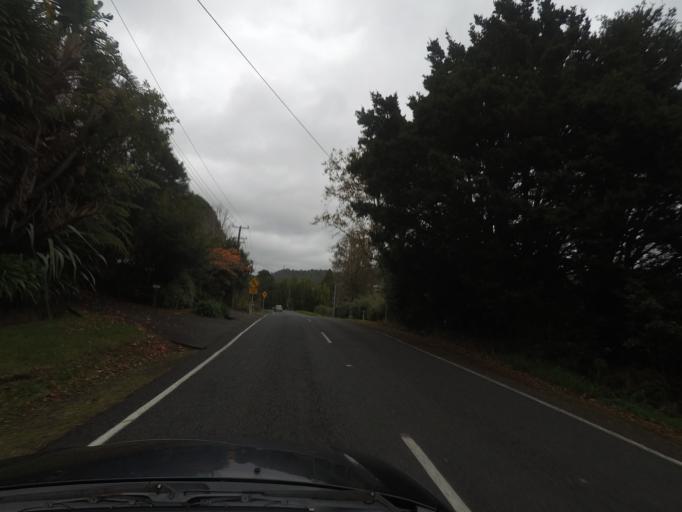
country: NZ
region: Auckland
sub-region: Auckland
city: Titirangi
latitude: -36.9281
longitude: 174.5946
